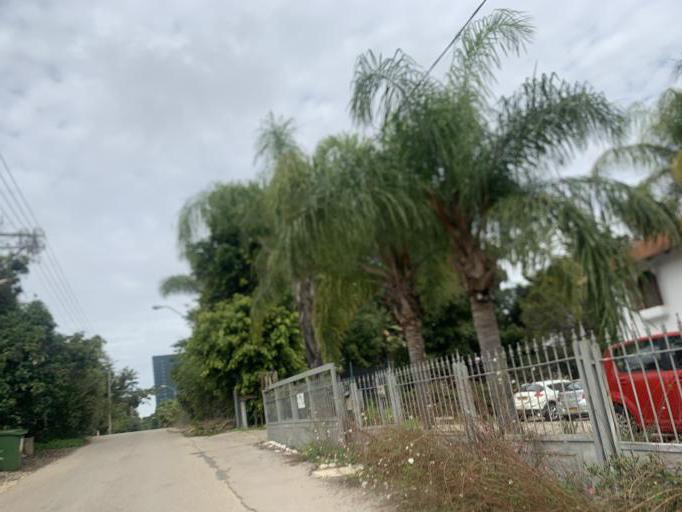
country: IL
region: Central District
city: Hod HaSharon
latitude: 32.1681
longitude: 34.8913
